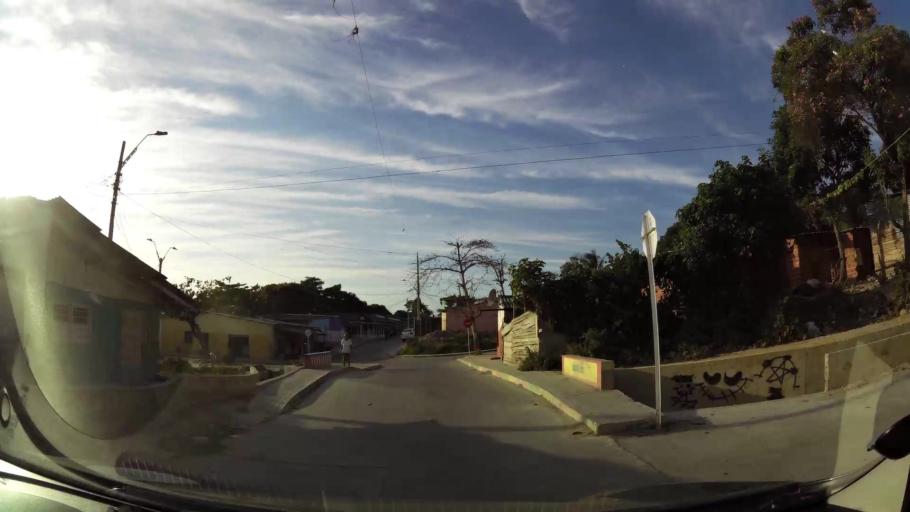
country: CO
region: Atlantico
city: Barranquilla
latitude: 10.9548
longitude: -74.8100
